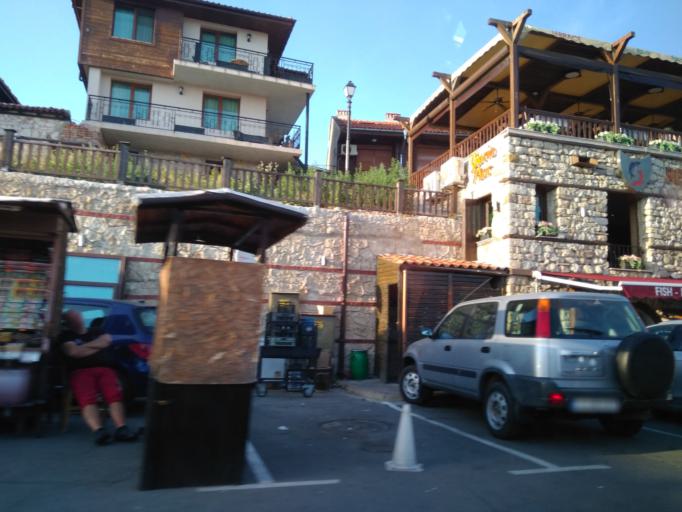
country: BG
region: Burgas
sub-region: Obshtina Nesebur
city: Nesebar
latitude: 42.6579
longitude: 27.7314
